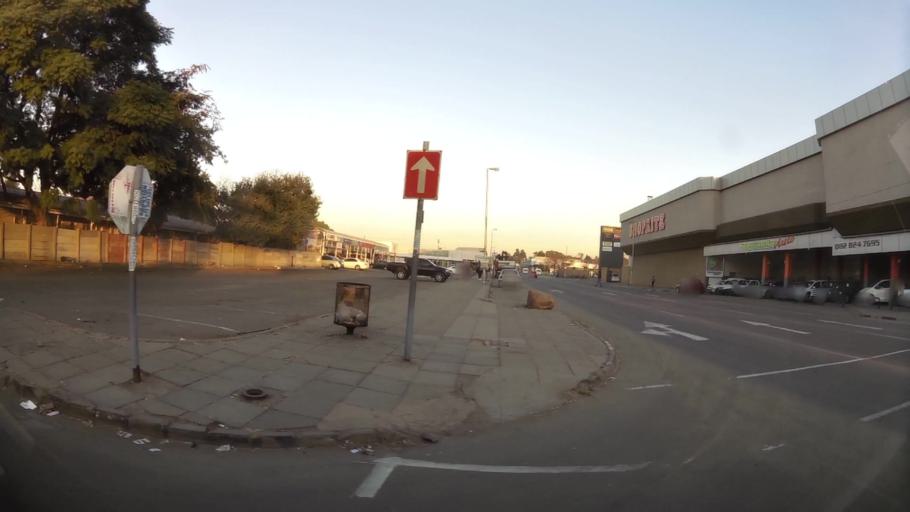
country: ZA
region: North-West
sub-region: Bojanala Platinum District Municipality
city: Rustenburg
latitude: -25.6671
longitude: 27.2439
